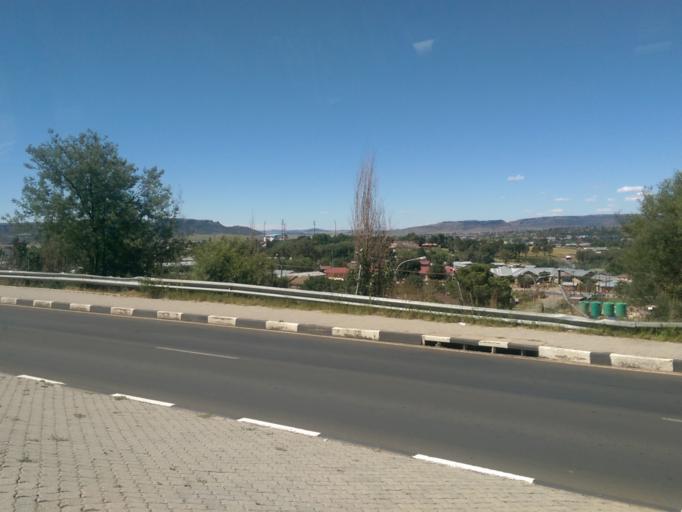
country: LS
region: Maseru
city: Maseru
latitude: -29.3242
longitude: 27.4963
